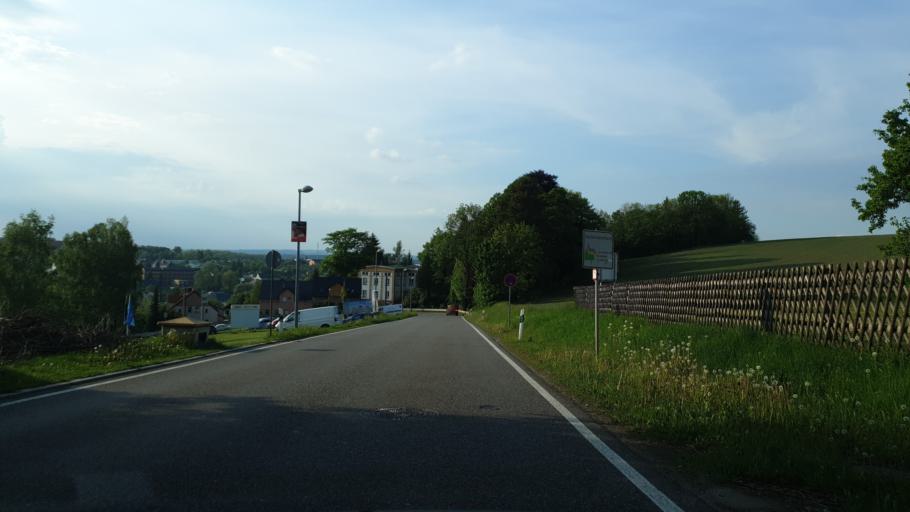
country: DE
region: Saxony
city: Stollberg
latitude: 50.7061
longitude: 12.7869
